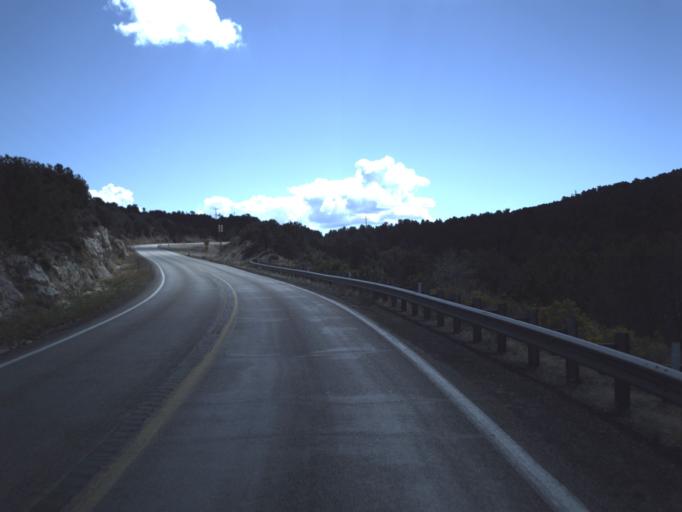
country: US
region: Utah
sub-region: Washington County
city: Enterprise
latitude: 37.5337
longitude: -113.6515
